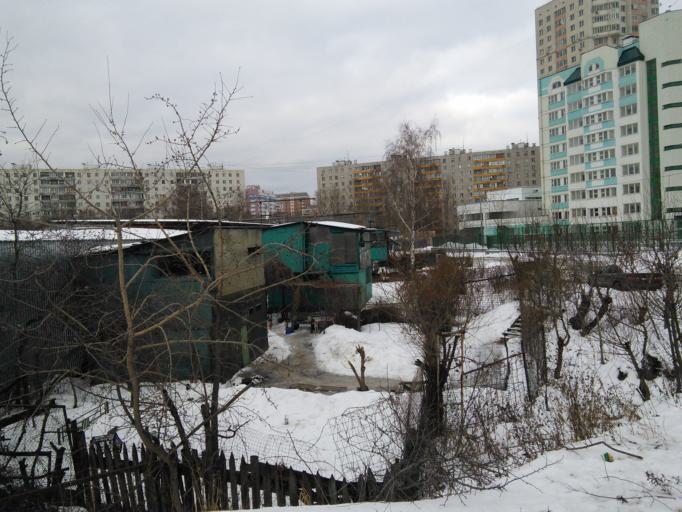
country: RU
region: Moscow
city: Zapadnoye Degunino
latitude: 55.8626
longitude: 37.5350
